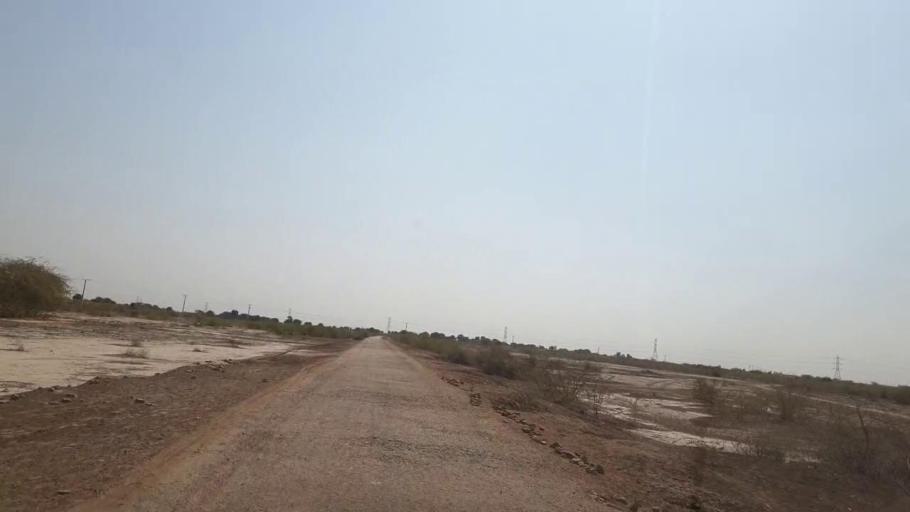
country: PK
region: Sindh
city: Nabisar
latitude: 25.0712
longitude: 69.5487
